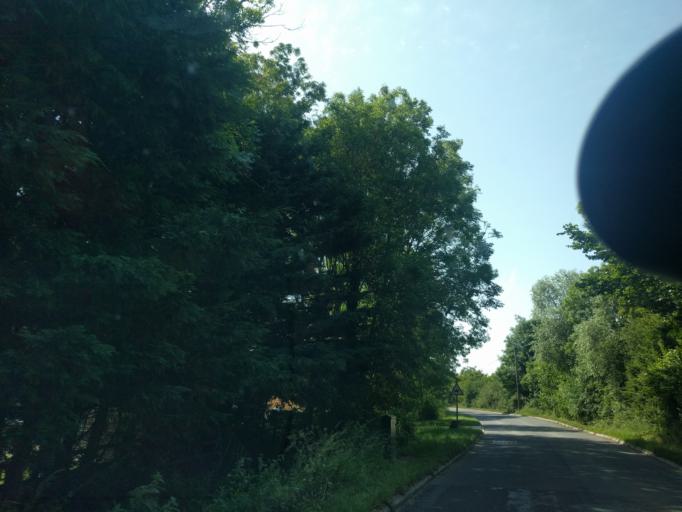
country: GB
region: England
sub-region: Wiltshire
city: Lyneham
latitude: 51.5337
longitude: -2.0023
